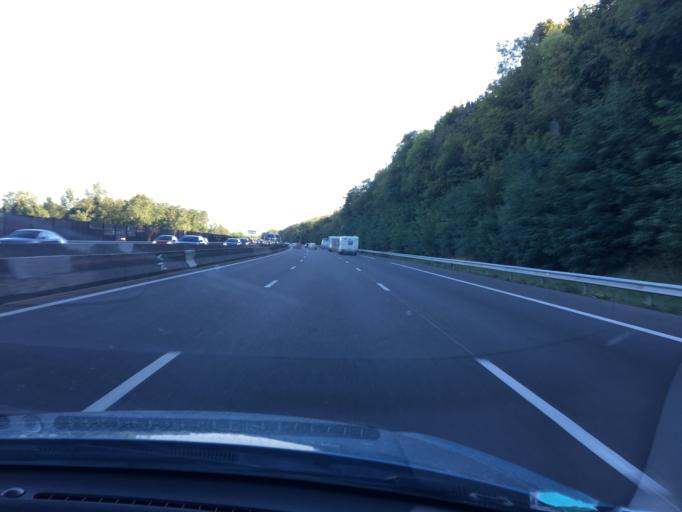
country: FR
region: Bourgogne
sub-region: Departement de Saone-et-Loire
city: Sance
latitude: 46.3634
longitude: 4.8313
